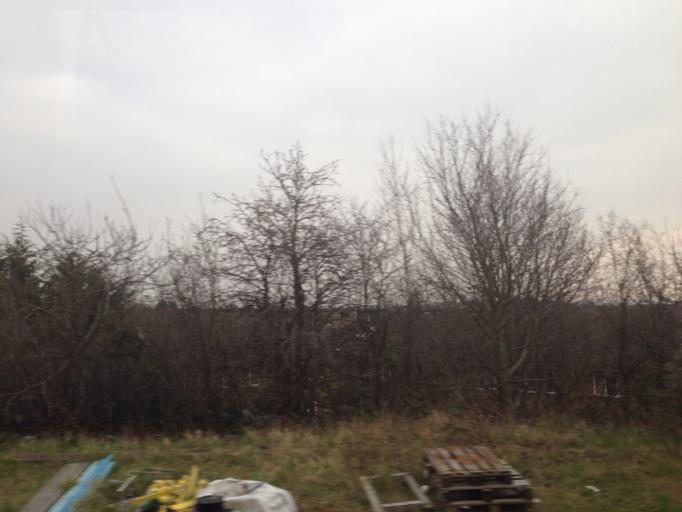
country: GB
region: England
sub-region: Greater London
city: Mitcham
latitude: 51.4187
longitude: -0.1412
